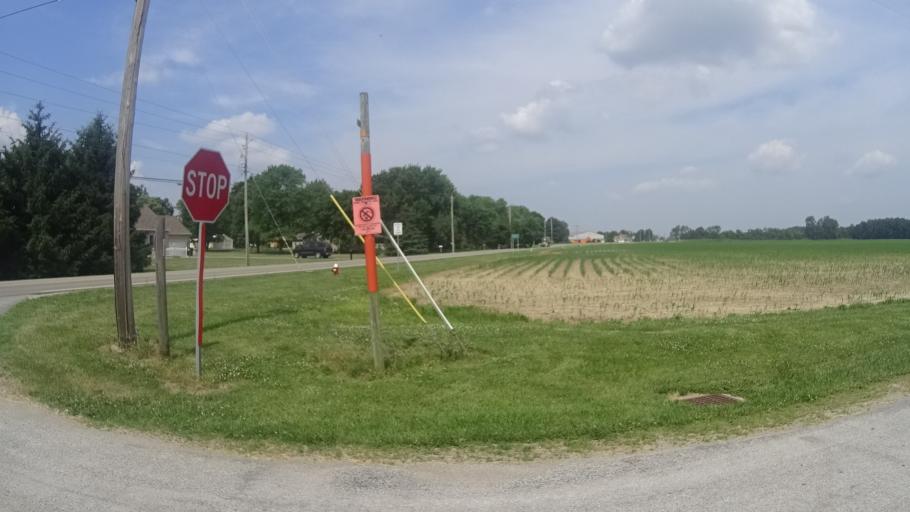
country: US
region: Ohio
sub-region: Erie County
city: Sandusky
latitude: 41.3487
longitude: -82.6941
